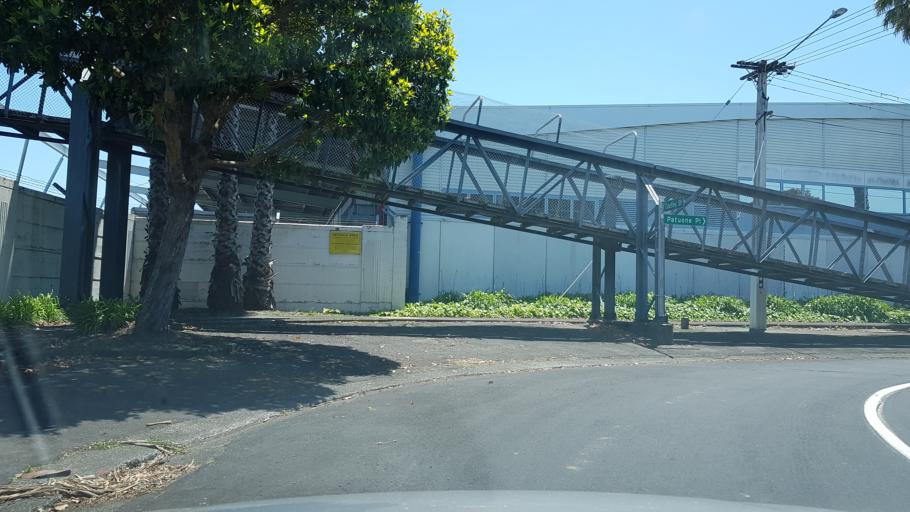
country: NZ
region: Auckland
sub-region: Auckland
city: Auckland
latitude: -36.8259
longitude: 174.7893
